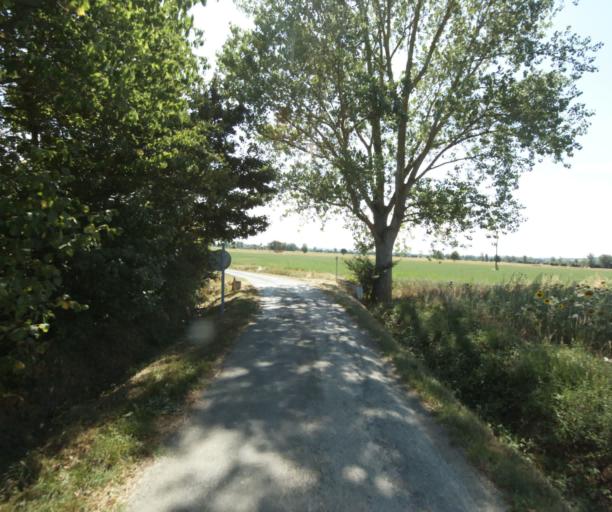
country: FR
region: Midi-Pyrenees
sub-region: Departement de la Haute-Garonne
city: Revel
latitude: 43.4966
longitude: 1.9952
